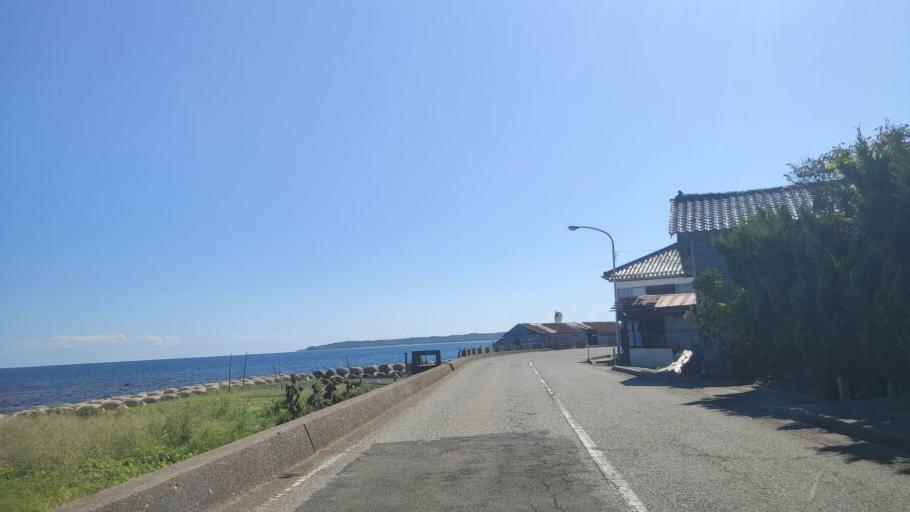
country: JP
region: Toyama
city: Nyuzen
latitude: 37.4977
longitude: 137.3496
